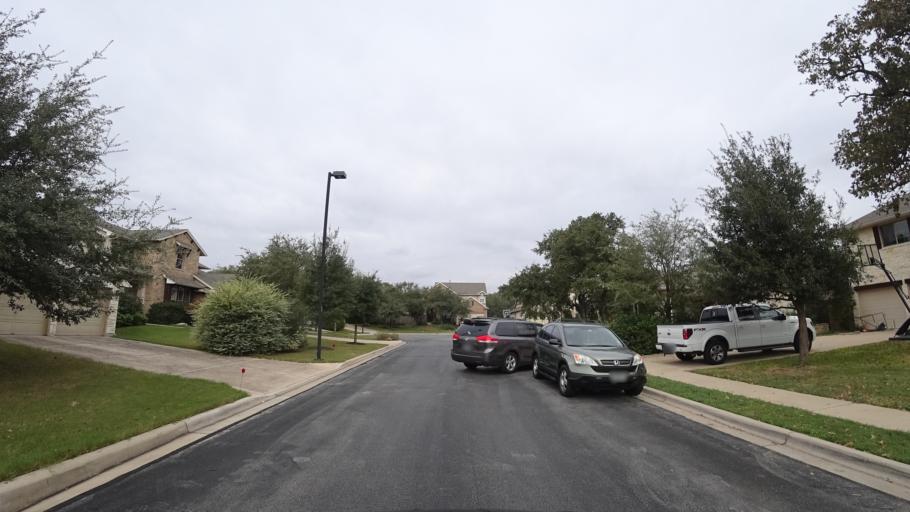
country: US
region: Texas
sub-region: Travis County
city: Shady Hollow
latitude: 30.1955
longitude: -97.9050
